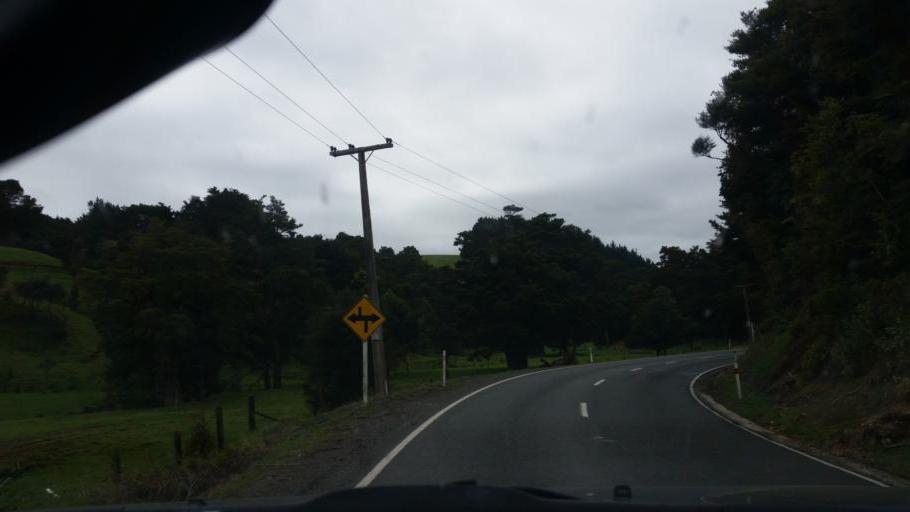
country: NZ
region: Northland
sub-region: Kaipara District
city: Dargaville
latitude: -35.8115
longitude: 173.7273
